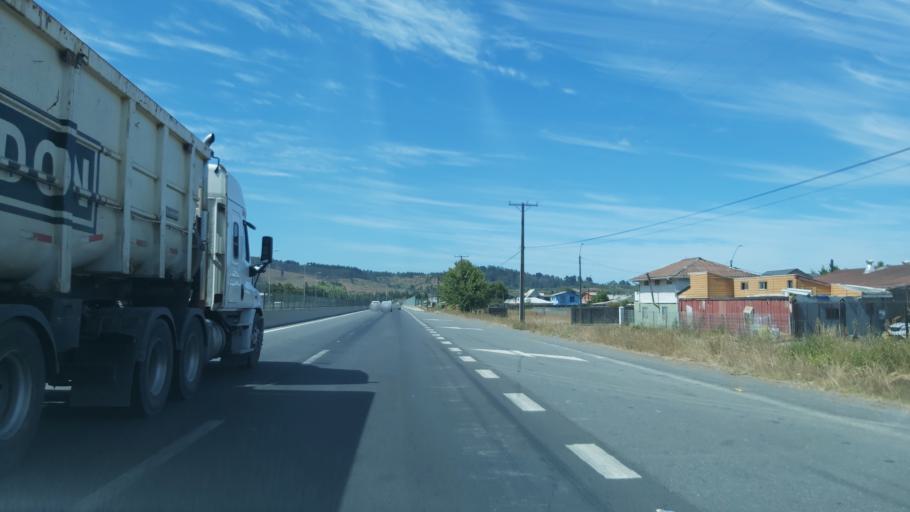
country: CL
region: Biobio
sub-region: Provincia de Concepcion
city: Coronel
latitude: -37.0338
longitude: -73.1349
